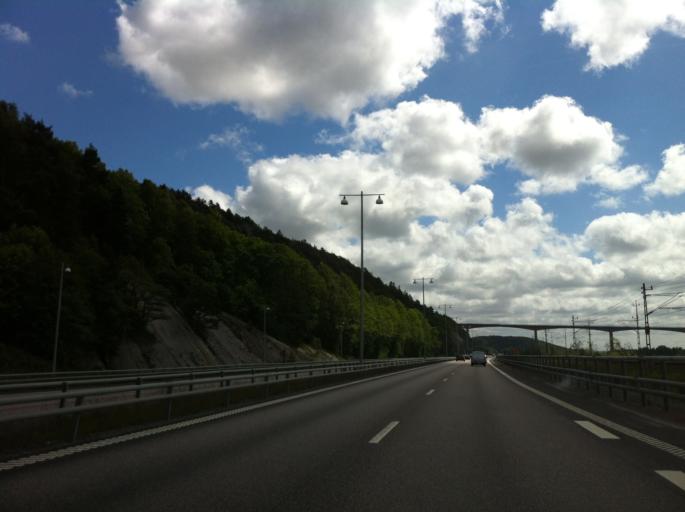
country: SE
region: Vaestra Goetaland
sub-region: Ale Kommun
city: Surte
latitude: 57.8521
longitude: 12.0143
